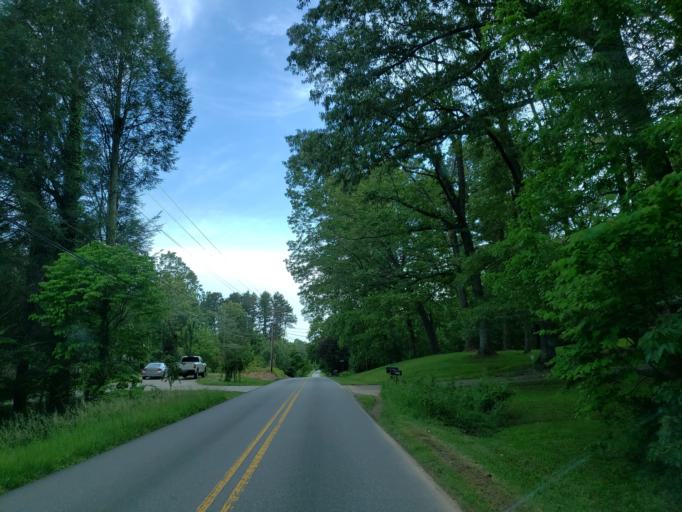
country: US
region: Georgia
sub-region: Fannin County
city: Blue Ridge
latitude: 34.8418
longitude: -84.3424
